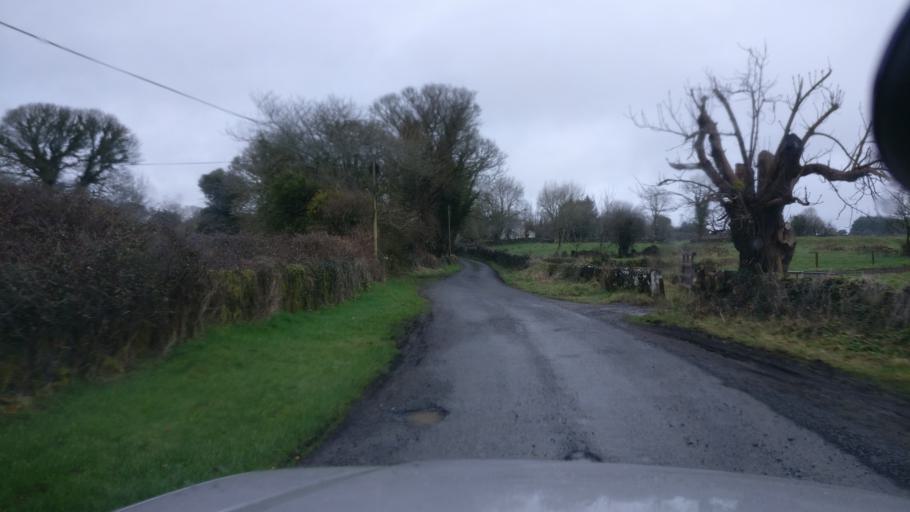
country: IE
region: Connaught
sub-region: County Galway
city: Loughrea
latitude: 53.1803
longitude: -8.6068
